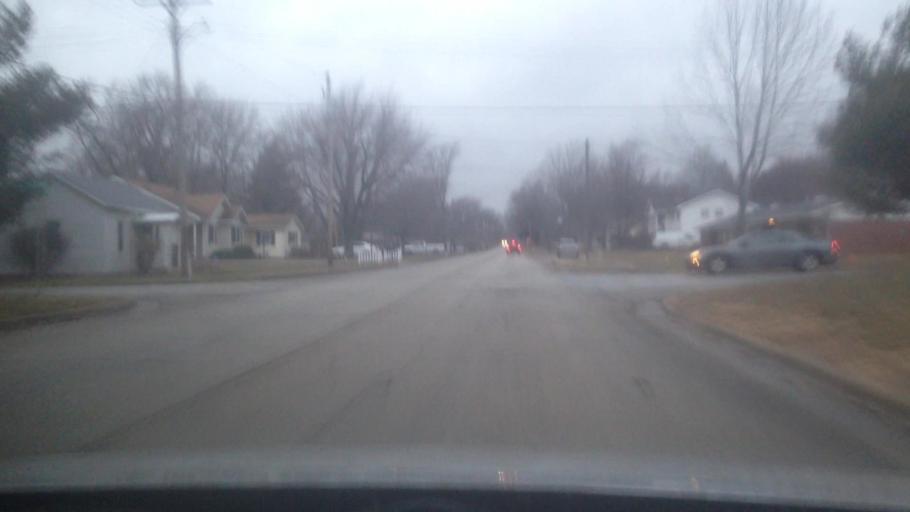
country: US
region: Illinois
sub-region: Christian County
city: Pana
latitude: 39.3831
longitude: -89.0696
